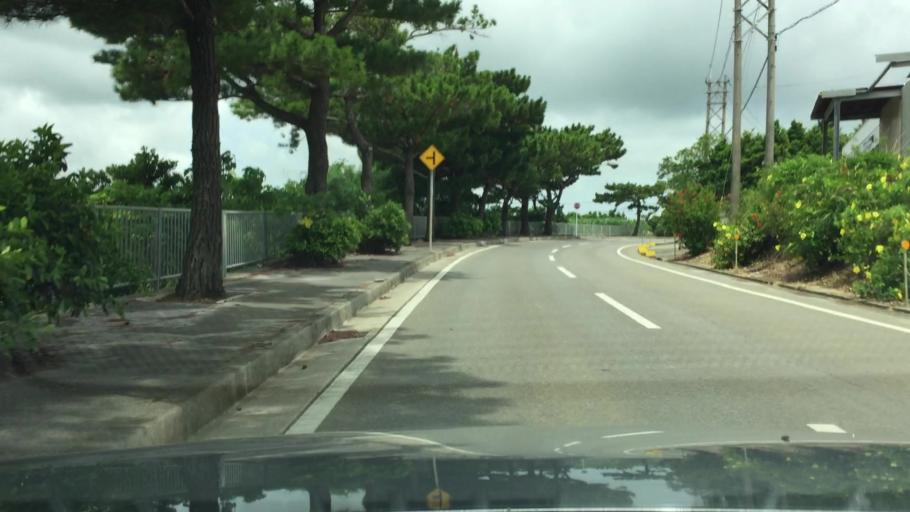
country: JP
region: Okinawa
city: Ishigaki
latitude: 24.3936
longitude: 124.1699
